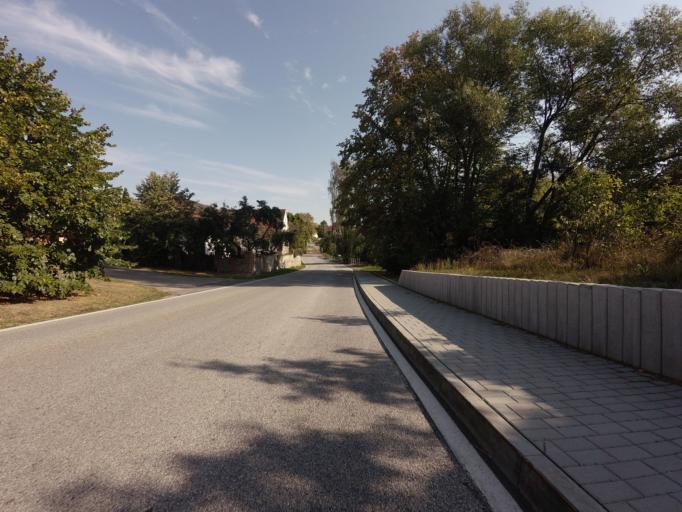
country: CZ
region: Jihocesky
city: Tyn nad Vltavou
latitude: 49.2793
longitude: 14.3984
